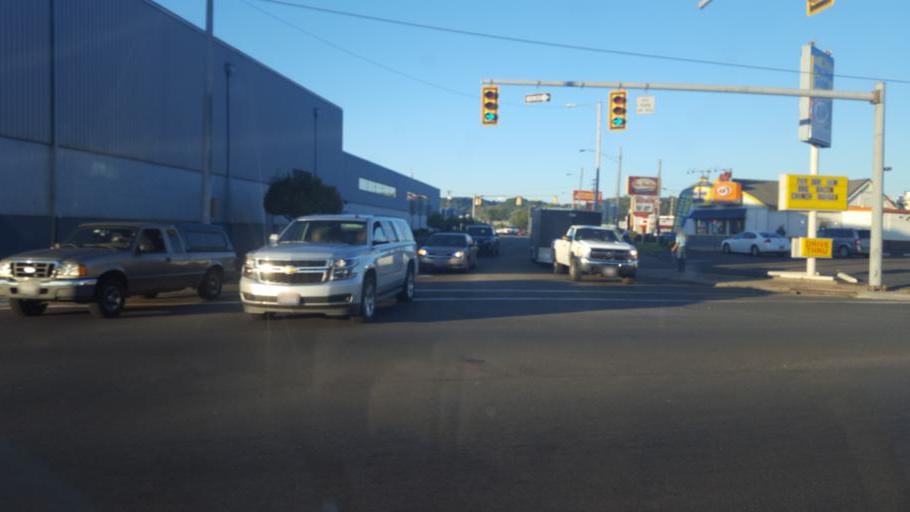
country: US
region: Ohio
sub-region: Scioto County
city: Portsmouth
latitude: 38.7392
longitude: -82.9961
